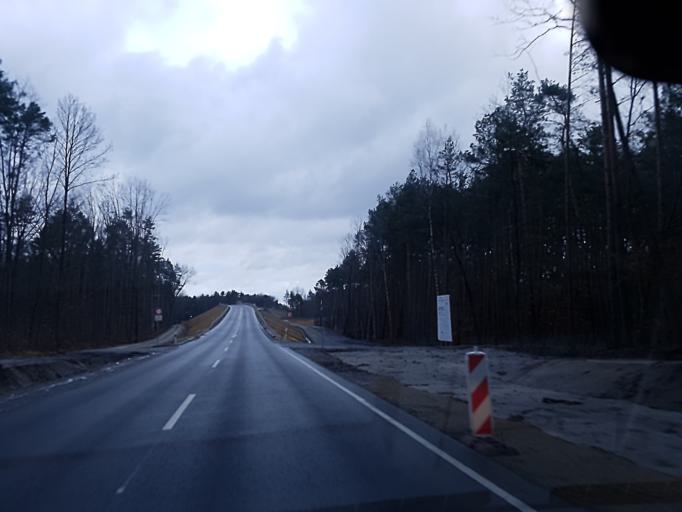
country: DE
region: Brandenburg
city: Hohenleipisch
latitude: 51.5196
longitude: 13.5735
